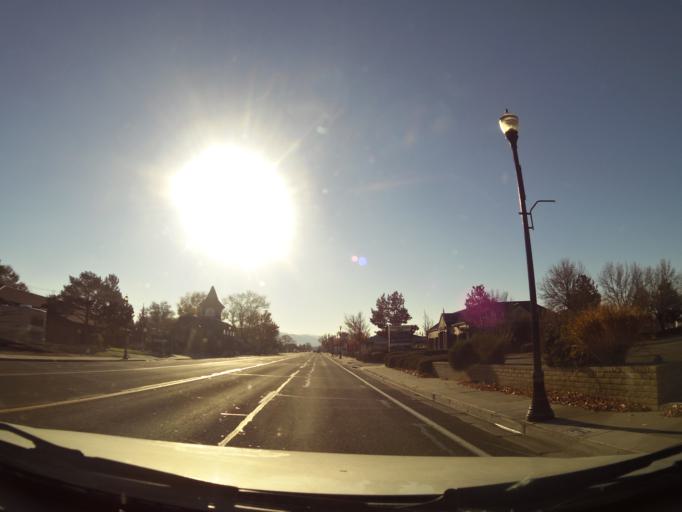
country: US
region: Nevada
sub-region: Douglas County
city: Minden
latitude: 38.9484
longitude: -119.7585
